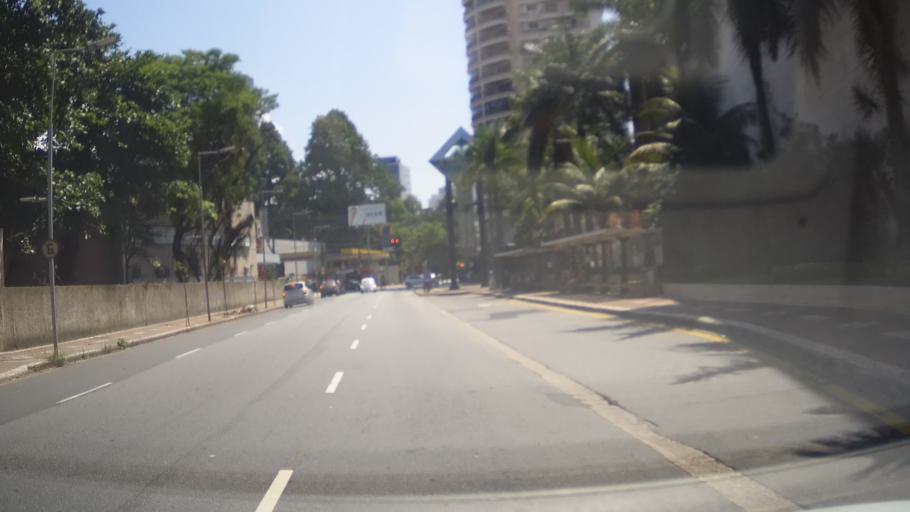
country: BR
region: Sao Paulo
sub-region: Santos
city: Santos
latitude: -23.9774
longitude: -46.3103
